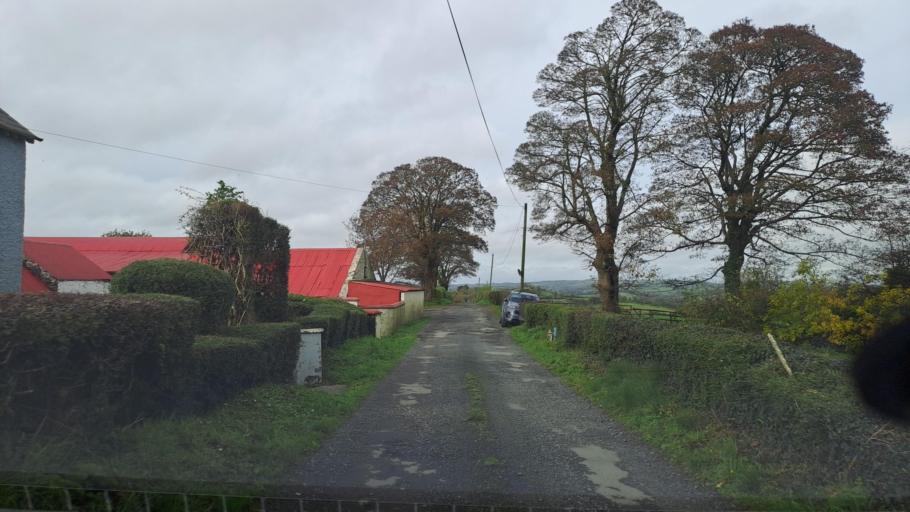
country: IE
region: Ulster
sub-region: County Monaghan
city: Carrickmacross
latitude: 54.0202
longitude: -6.8211
